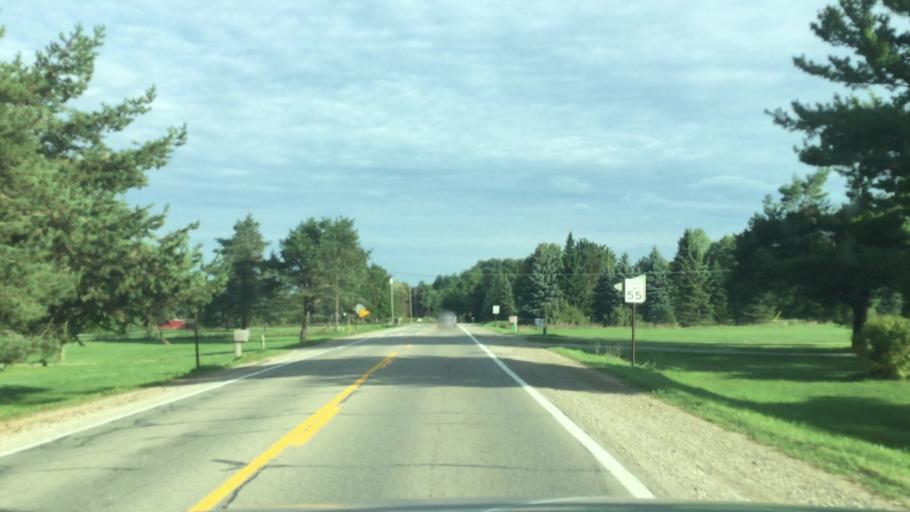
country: US
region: Michigan
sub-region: Livingston County
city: Brighton
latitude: 42.4933
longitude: -83.8592
